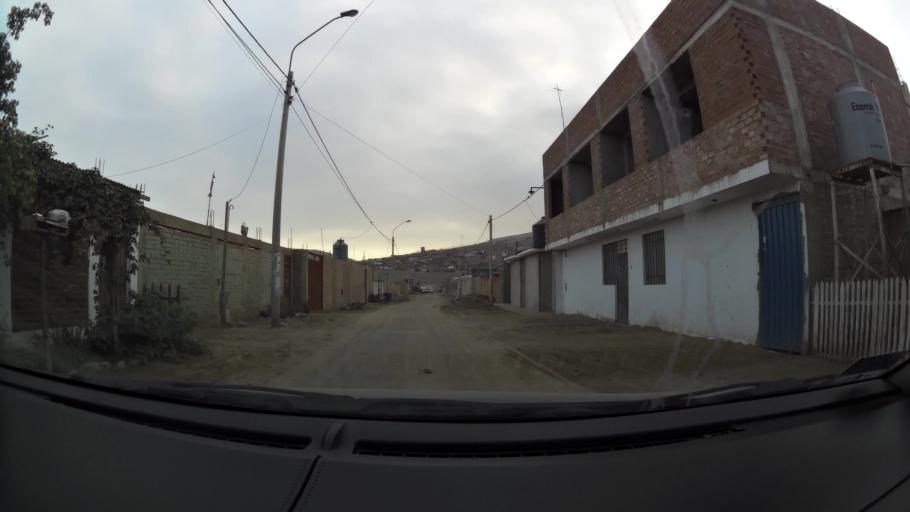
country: PE
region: Lima
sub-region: Lima
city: Santa Rosa
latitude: -11.7331
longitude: -77.1429
